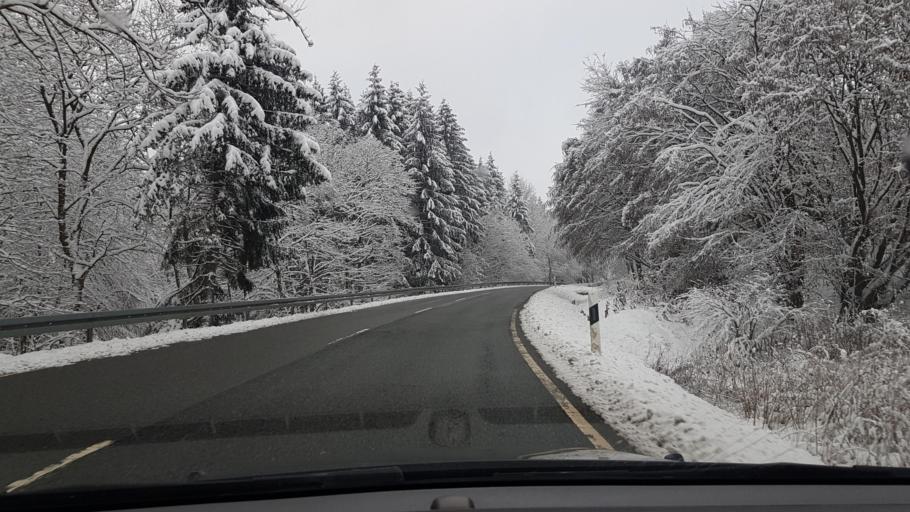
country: DE
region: Lower Saxony
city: Clausthal-Zellerfeld
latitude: 51.8052
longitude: 10.3196
